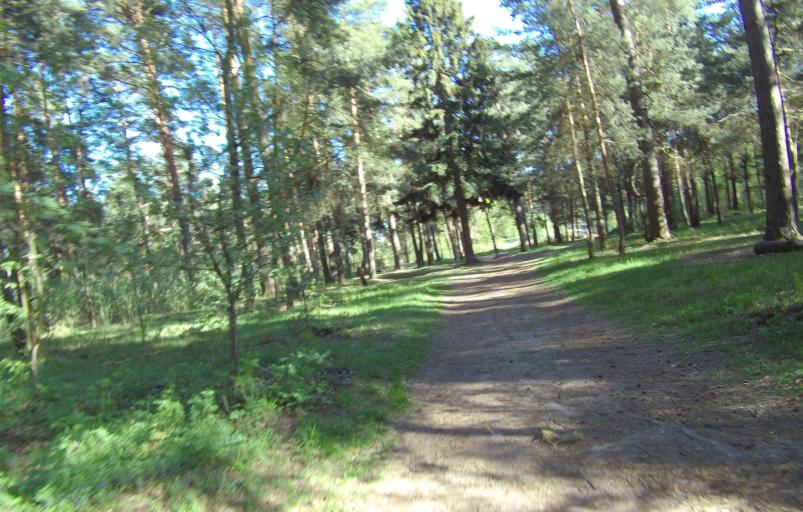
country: RU
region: Moskovskaya
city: Kratovo
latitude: 55.5609
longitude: 38.1871
